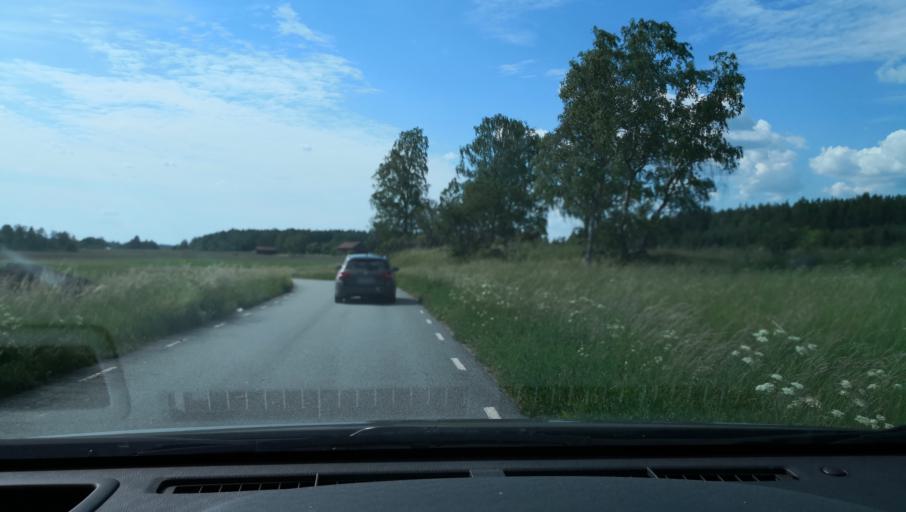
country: SE
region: Uppsala
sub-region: Enkopings Kommun
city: Orsundsbro
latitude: 59.8162
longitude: 17.3538
